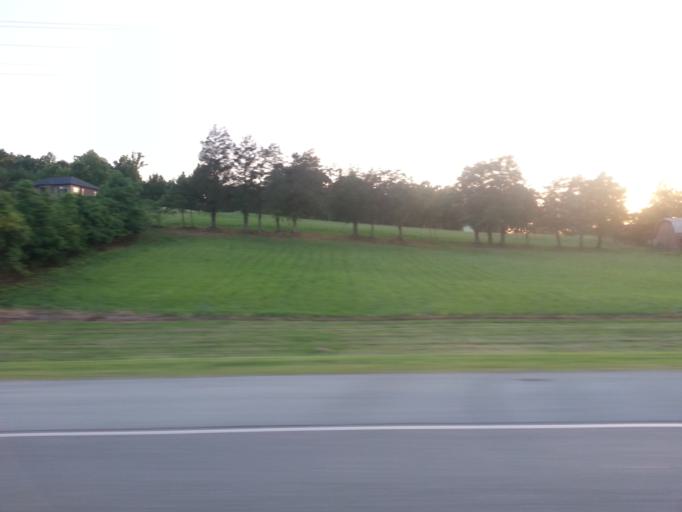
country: US
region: Tennessee
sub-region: Monroe County
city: Madisonville
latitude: 35.3639
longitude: -84.3008
